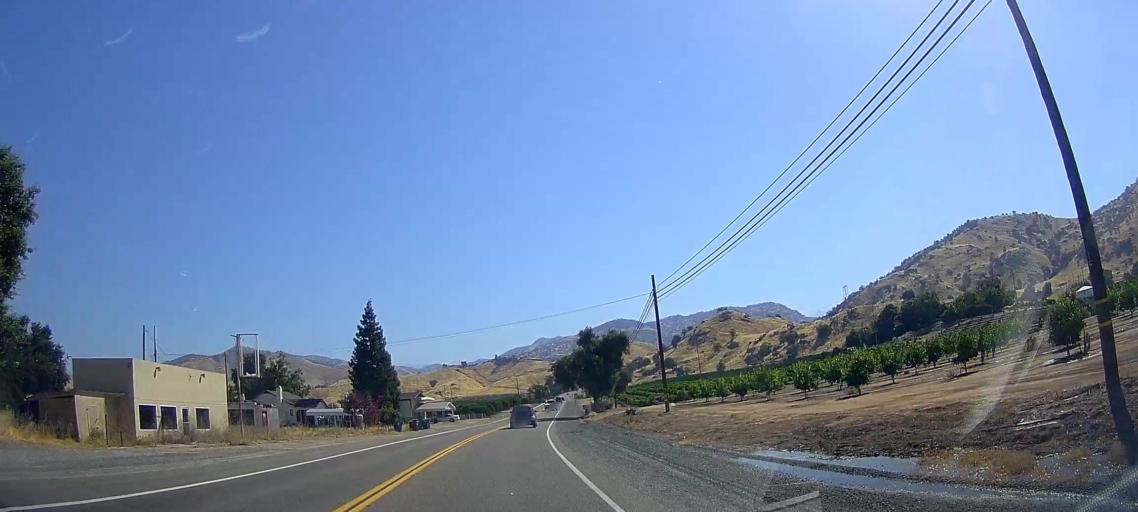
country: US
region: California
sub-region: Tulare County
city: Woodlake
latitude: 36.3962
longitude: -119.0208
